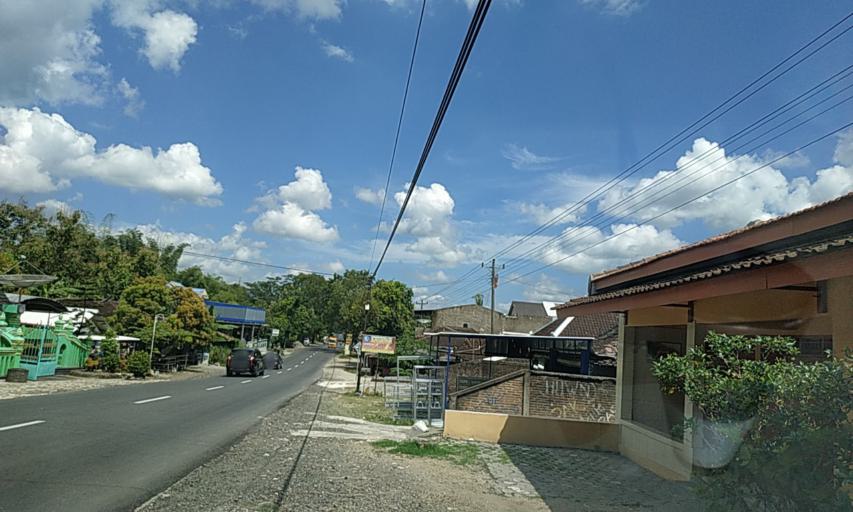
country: ID
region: East Java
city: Ploso
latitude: -7.9988
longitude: 110.9356
